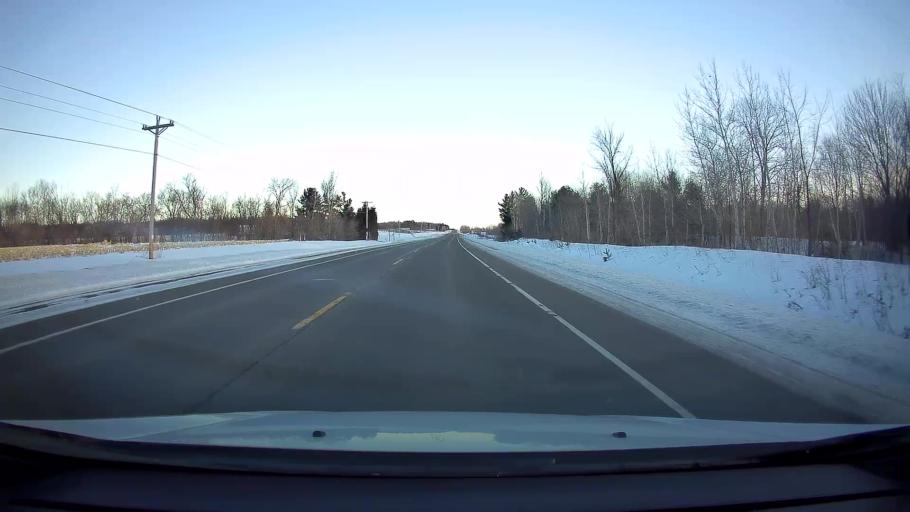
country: US
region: Wisconsin
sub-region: Barron County
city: Cumberland
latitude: 45.6117
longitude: -92.0094
